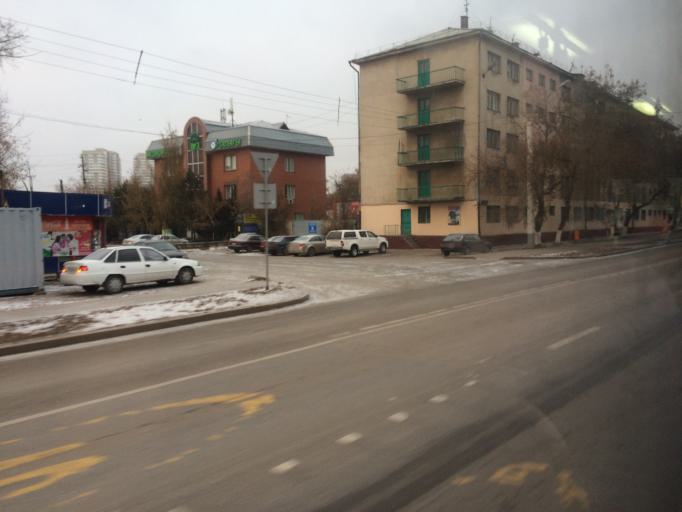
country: KZ
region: Astana Qalasy
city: Astana
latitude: 51.1663
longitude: 71.4521
